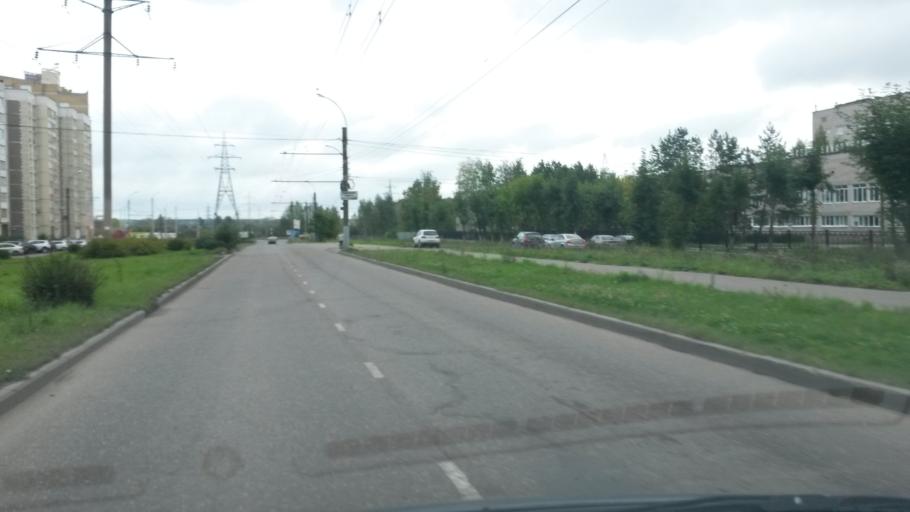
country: RU
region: Ivanovo
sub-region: Gorod Ivanovo
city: Ivanovo
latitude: 56.9590
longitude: 41.0257
